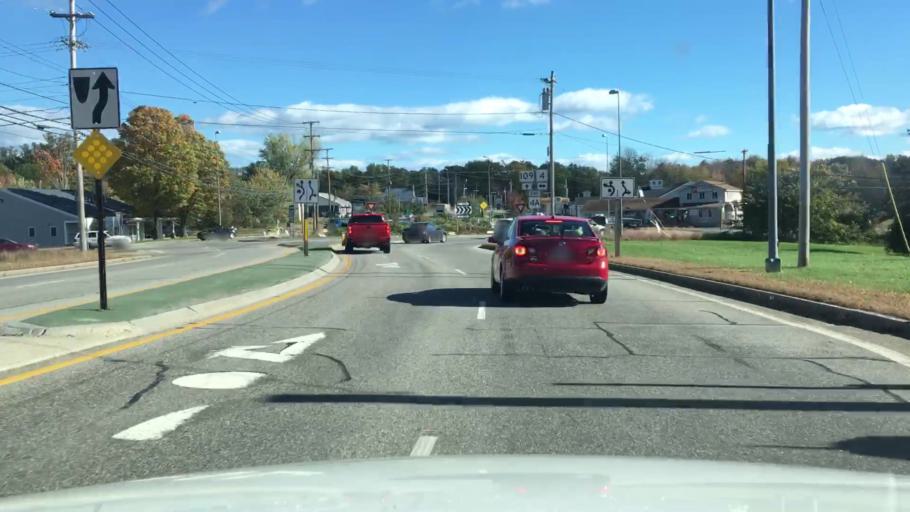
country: US
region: Maine
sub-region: York County
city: South Sanford
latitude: 43.4115
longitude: -70.7433
